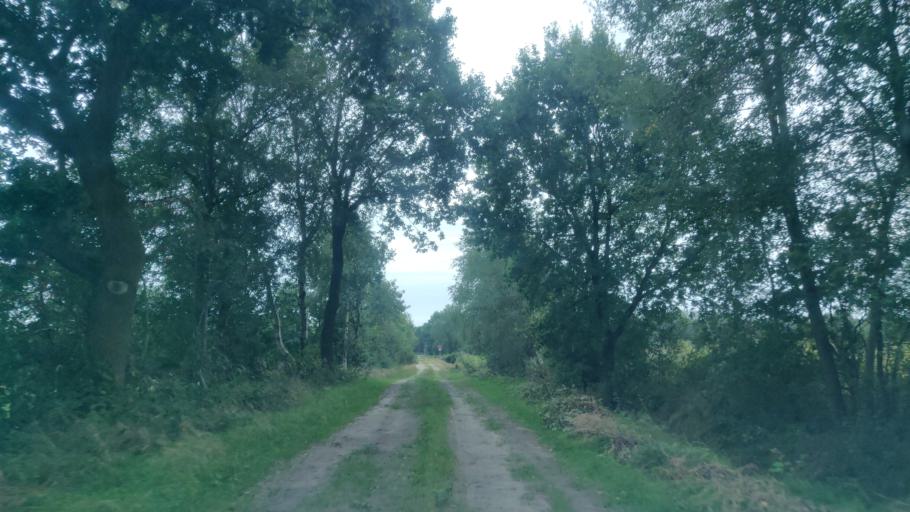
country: DE
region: Lower Saxony
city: Aurich
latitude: 53.5299
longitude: 7.4775
